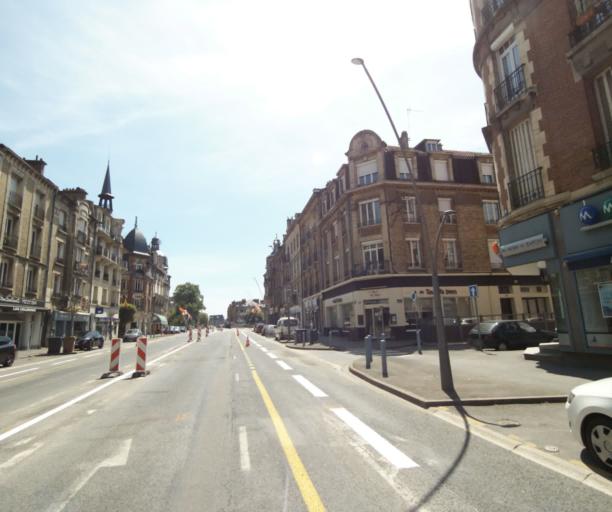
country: FR
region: Champagne-Ardenne
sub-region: Departement des Ardennes
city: Charleville-Mezieres
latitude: 49.7635
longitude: 4.7193
